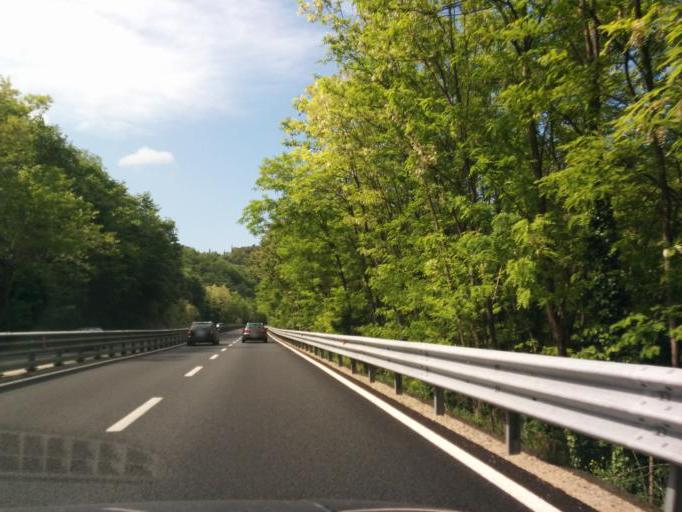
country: IT
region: Tuscany
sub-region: Province of Florence
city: Barberino Val d'Elsa
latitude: 43.5036
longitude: 11.1881
